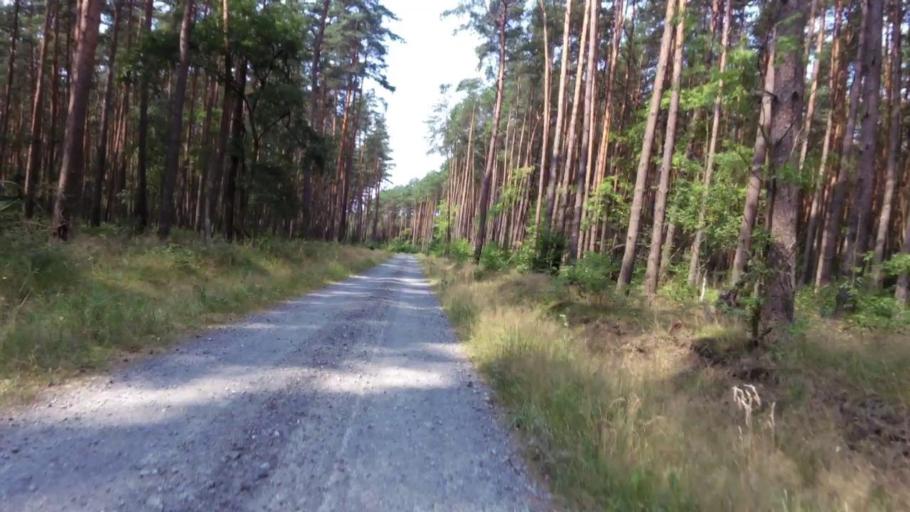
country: PL
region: West Pomeranian Voivodeship
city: Trzcinsko Zdroj
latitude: 52.8484
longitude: 14.6054
